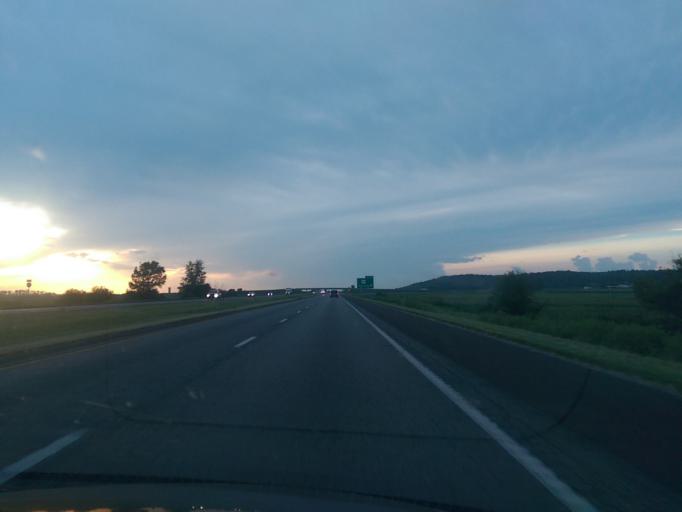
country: US
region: Missouri
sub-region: Atchison County
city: Rock Port
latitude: 40.2578
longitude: -95.4473
